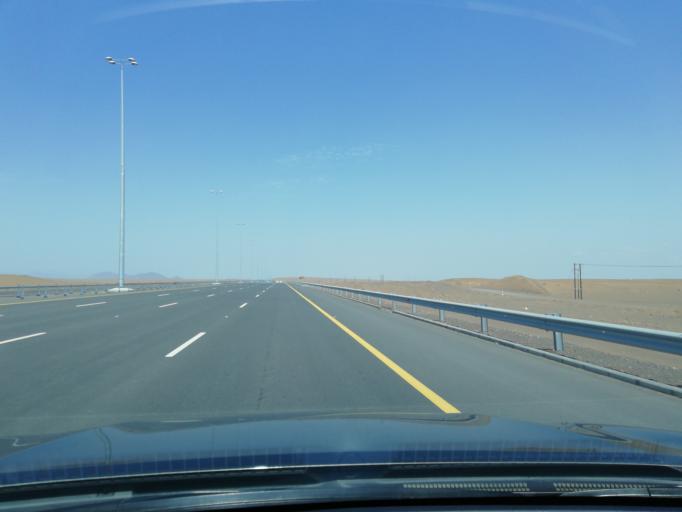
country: OM
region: Al Batinah
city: Rustaq
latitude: 23.5230
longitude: 57.6110
